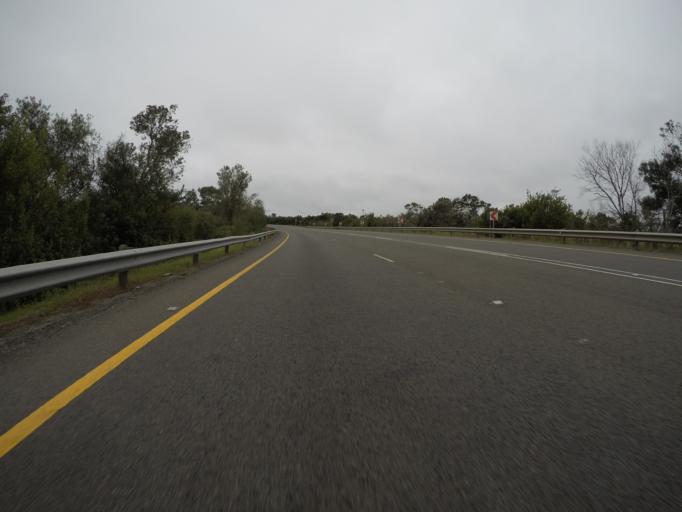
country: ZA
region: Western Cape
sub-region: Eden District Municipality
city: Plettenberg Bay
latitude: -33.9983
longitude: 23.4343
